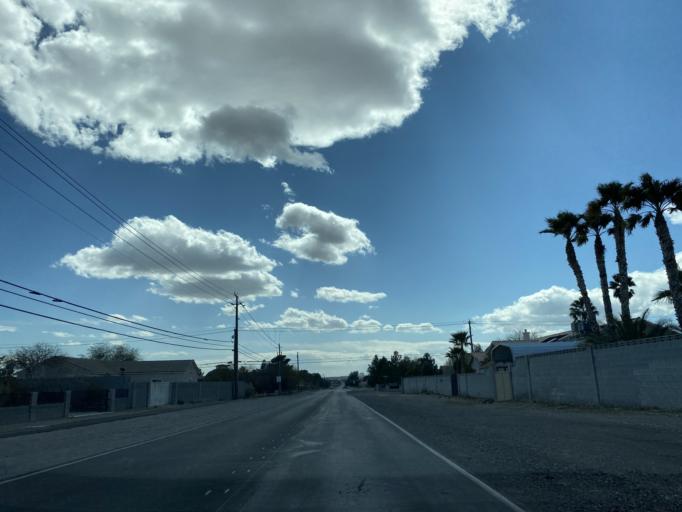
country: US
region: Nevada
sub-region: Clark County
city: Summerlin South
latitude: 36.2567
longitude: -115.2884
